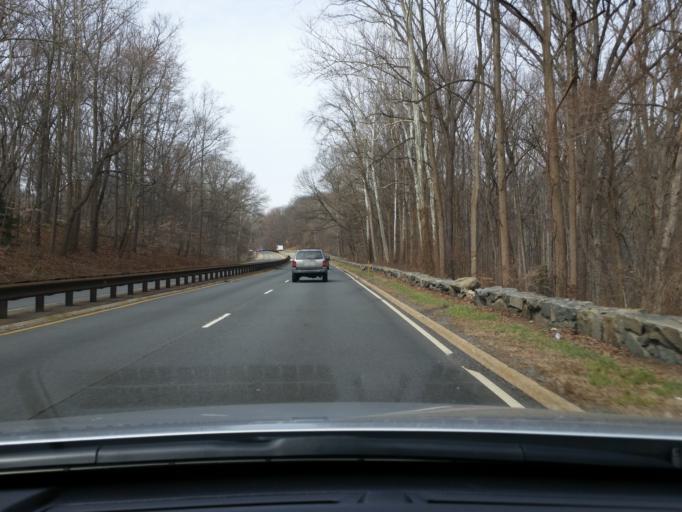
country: US
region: Maryland
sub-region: Montgomery County
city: Brookmont
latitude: 38.9307
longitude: -77.1216
